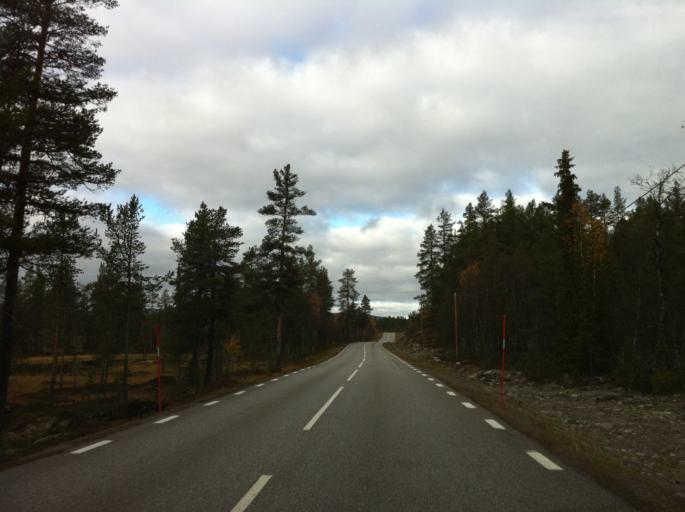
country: NO
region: Hedmark
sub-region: Engerdal
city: Engerdal
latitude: 62.0039
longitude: 12.4170
